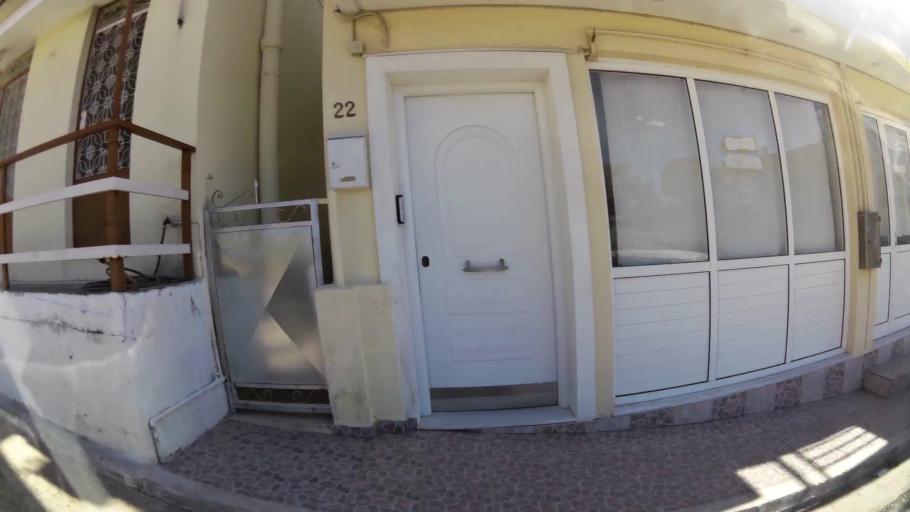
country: GR
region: Attica
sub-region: Nomos Piraios
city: Keratsini
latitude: 37.9656
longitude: 23.6069
